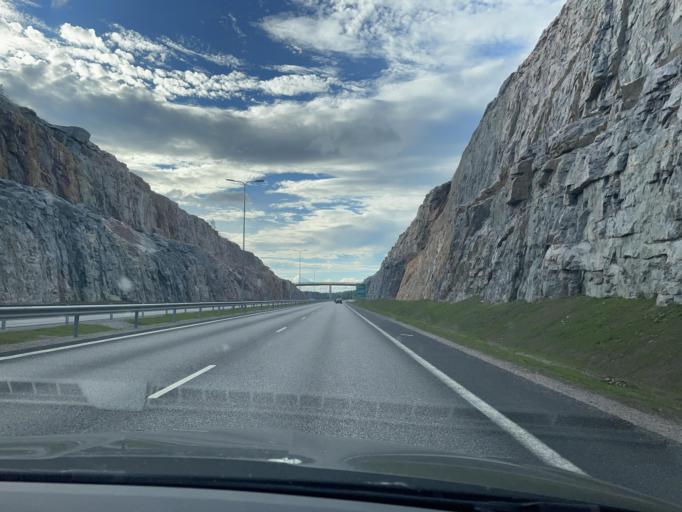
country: FI
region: Central Finland
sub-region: Jyvaeskylae
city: Jyvaeskylae
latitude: 62.3086
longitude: 25.7084
